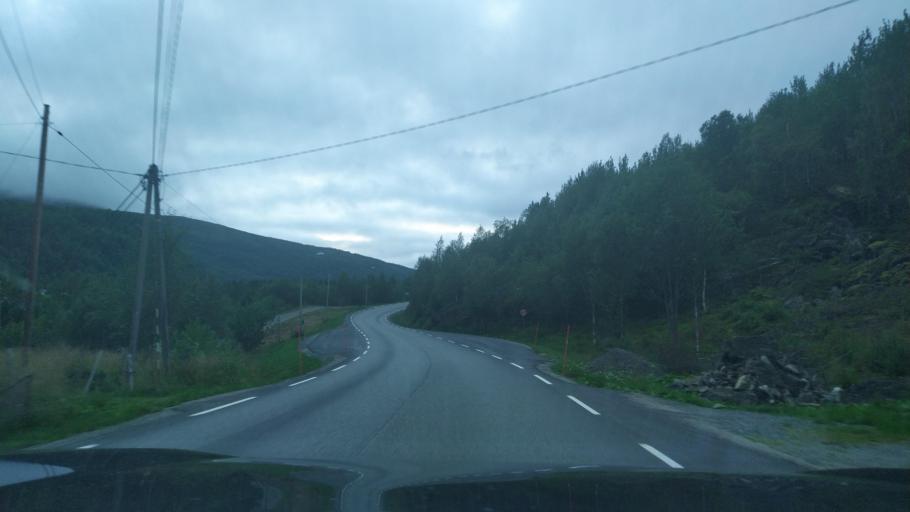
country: NO
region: Troms
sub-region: Lavangen
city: Tennevoll
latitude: 68.7248
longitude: 17.8373
